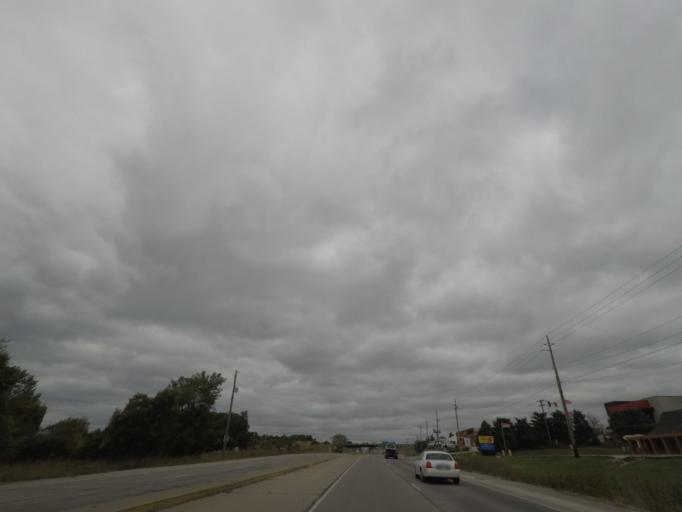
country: US
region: Iowa
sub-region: Polk County
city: Saylorville
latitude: 41.6453
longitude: -93.6005
